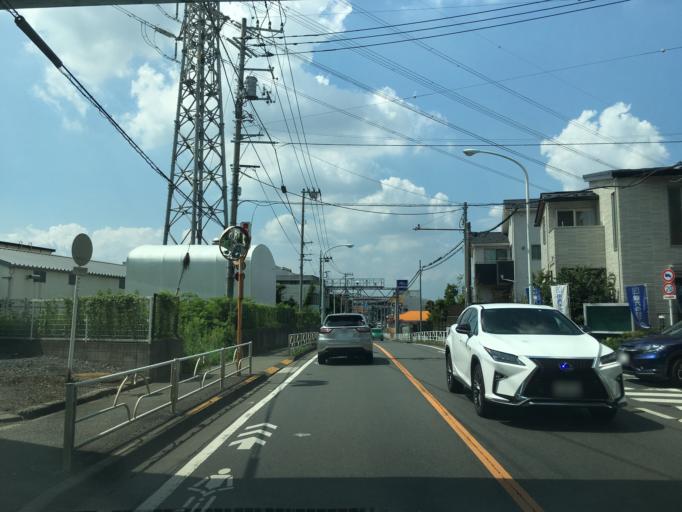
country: JP
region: Tokyo
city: Higashimurayama-shi
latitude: 35.7656
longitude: 139.4919
